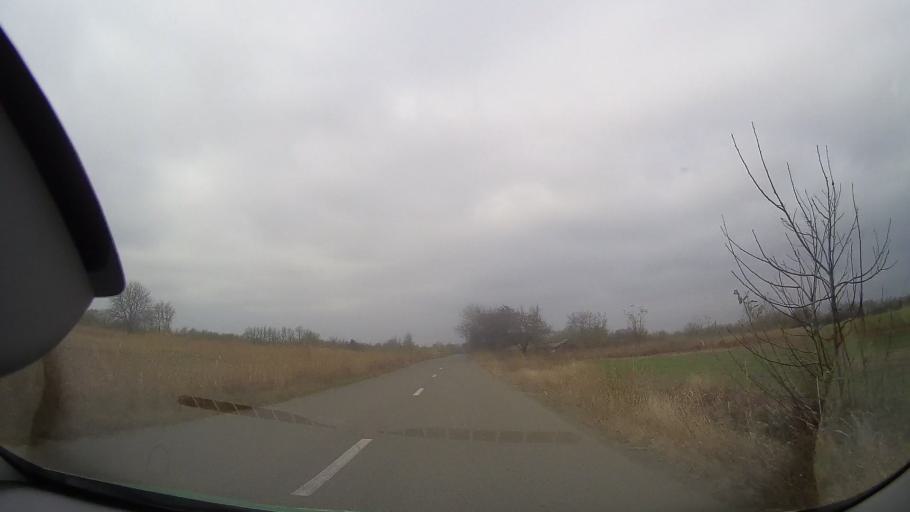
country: RO
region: Buzau
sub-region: Comuna Scutelnici
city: Scutelnici
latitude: 44.8746
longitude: 26.8837
